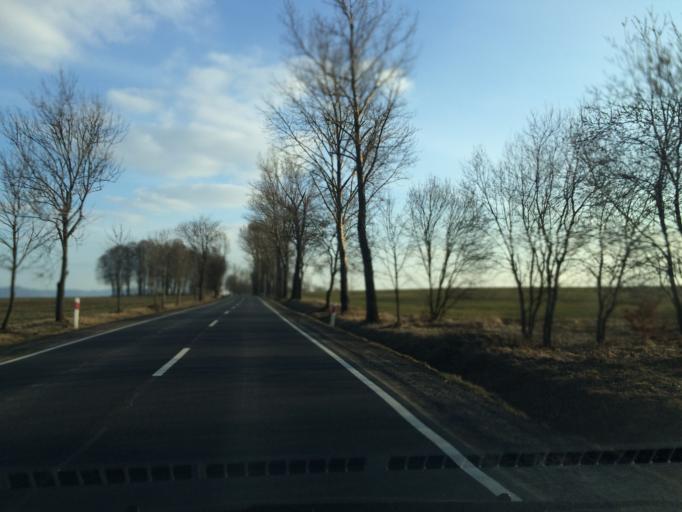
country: PL
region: Lower Silesian Voivodeship
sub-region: Powiat klodzki
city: Bystrzyca Klodzka
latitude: 50.2351
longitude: 16.6764
